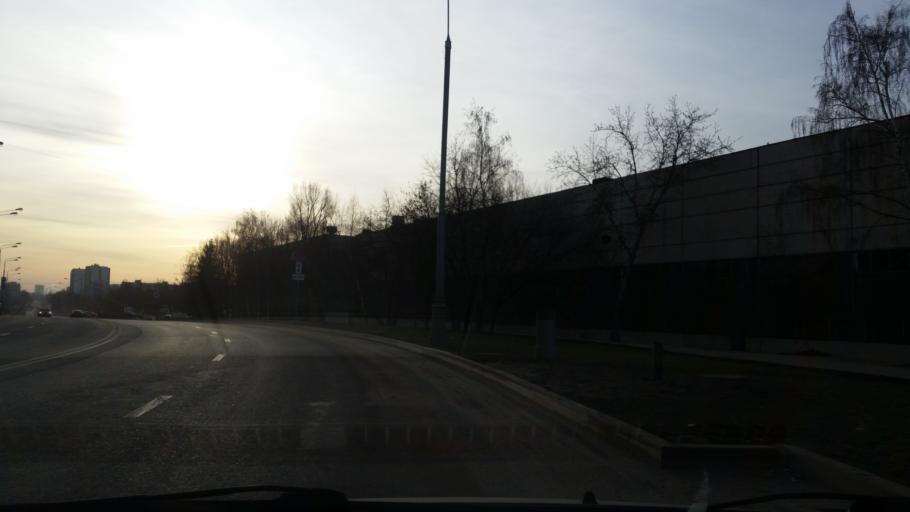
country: RU
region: Moscow
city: Tsaritsyno
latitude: 55.6121
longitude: 37.6270
